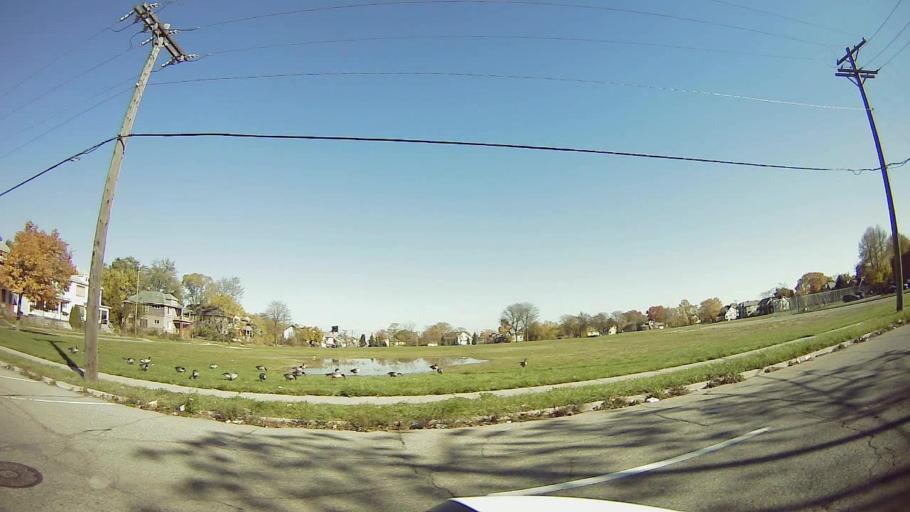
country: US
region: Michigan
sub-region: Wayne County
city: Highland Park
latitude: 42.3943
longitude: -83.1154
